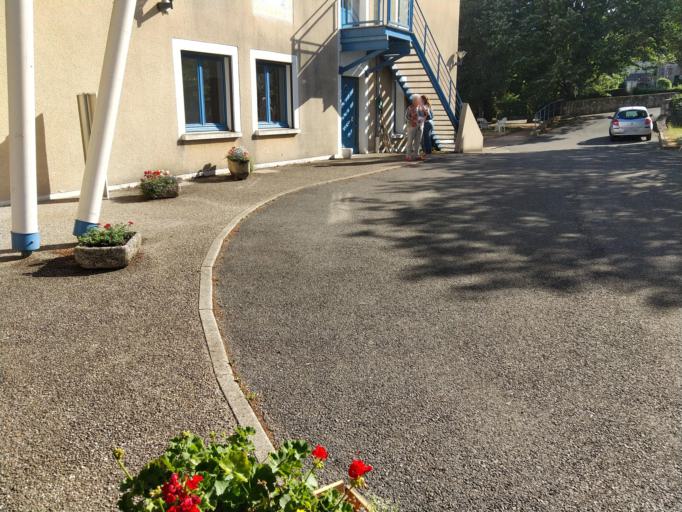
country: FR
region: Rhone-Alpes
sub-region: Departement de la Loire
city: Pelussin
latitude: 45.4249
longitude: 4.6806
